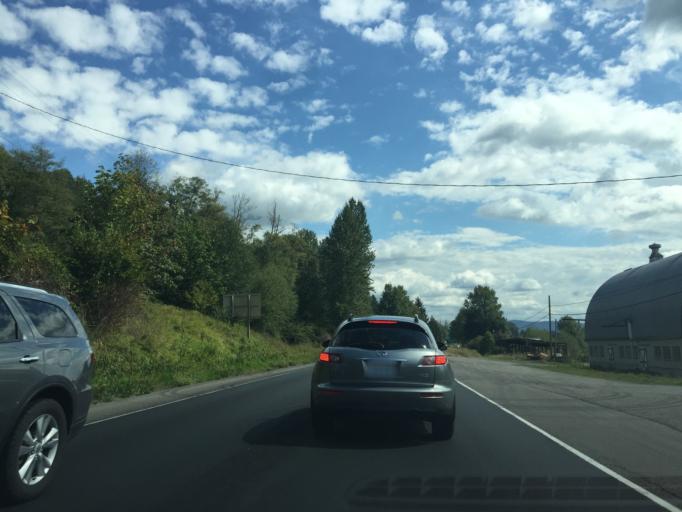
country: US
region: Washington
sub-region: Snohomish County
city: Snohomish
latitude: 47.9086
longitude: -122.0483
